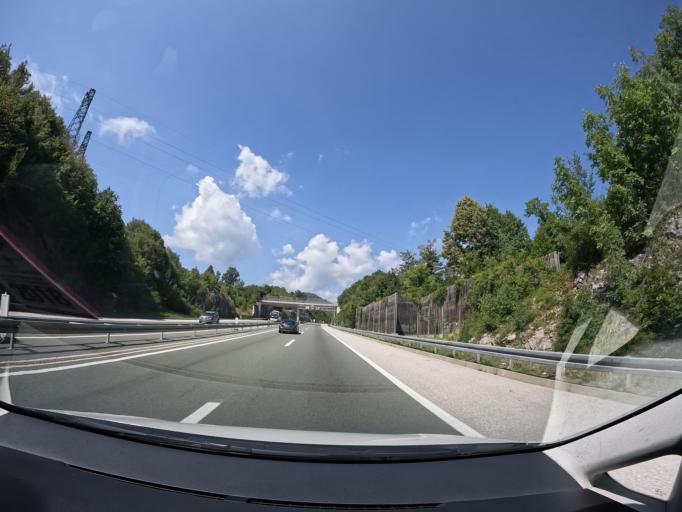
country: HR
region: Primorsko-Goranska
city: Matulji
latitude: 45.3770
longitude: 14.3143
